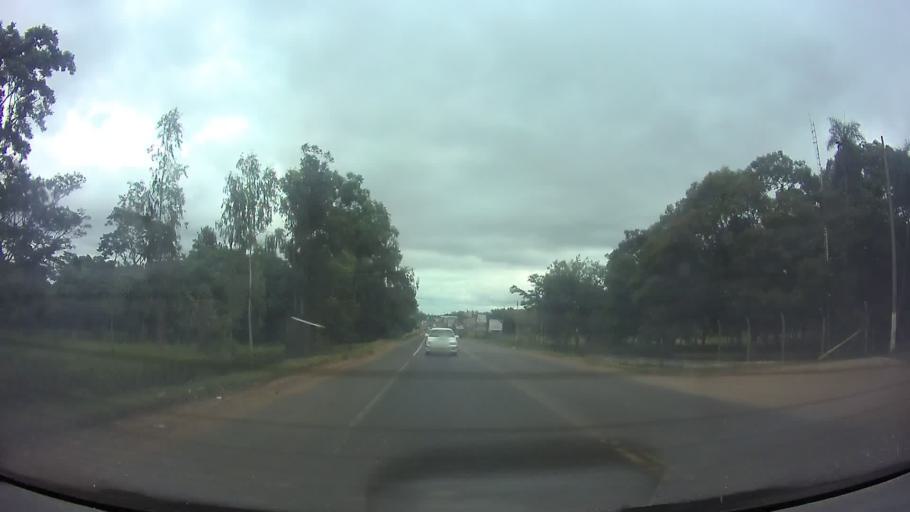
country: PY
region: Central
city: San Antonio
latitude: -25.4568
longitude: -57.5174
